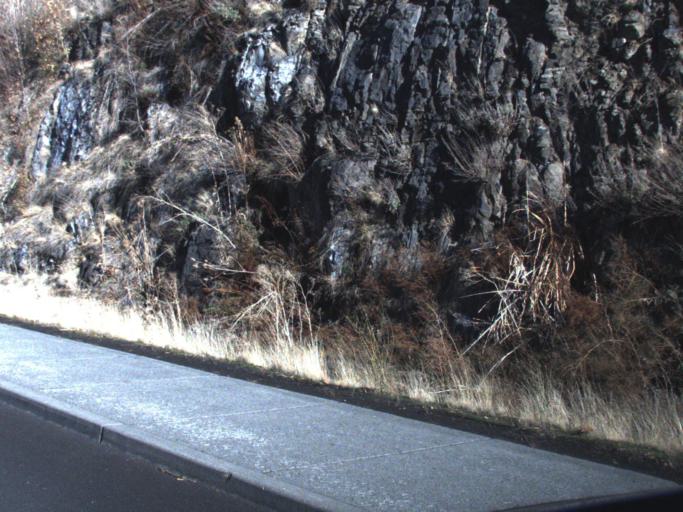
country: US
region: Washington
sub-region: Whitman County
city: Pullman
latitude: 46.7237
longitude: -117.1650
